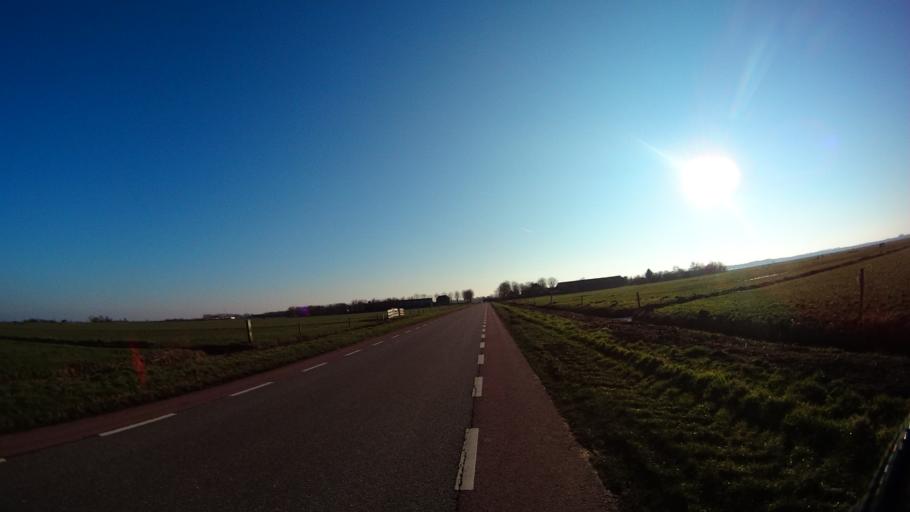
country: NL
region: Utrecht
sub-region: Gemeente Baarn
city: Baarn
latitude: 52.2381
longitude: 5.3013
